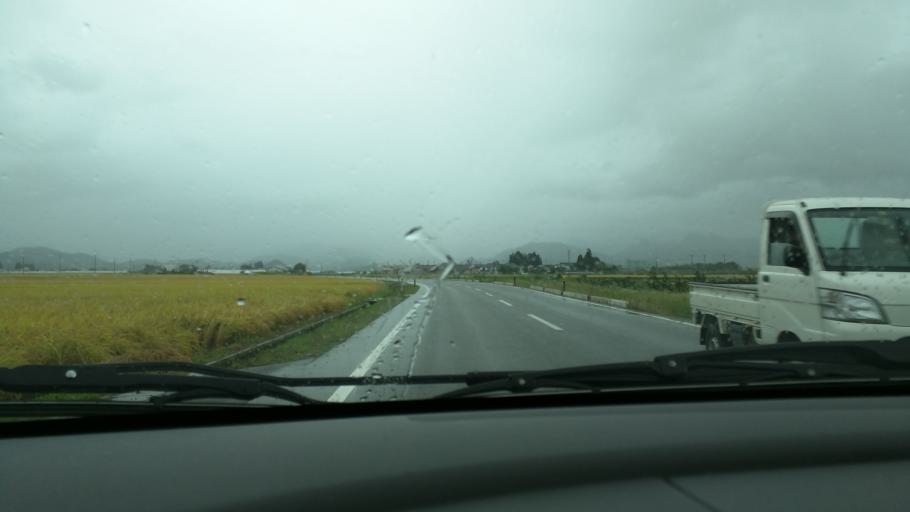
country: JP
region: Fukushima
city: Kitakata
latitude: 37.4853
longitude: 139.8574
